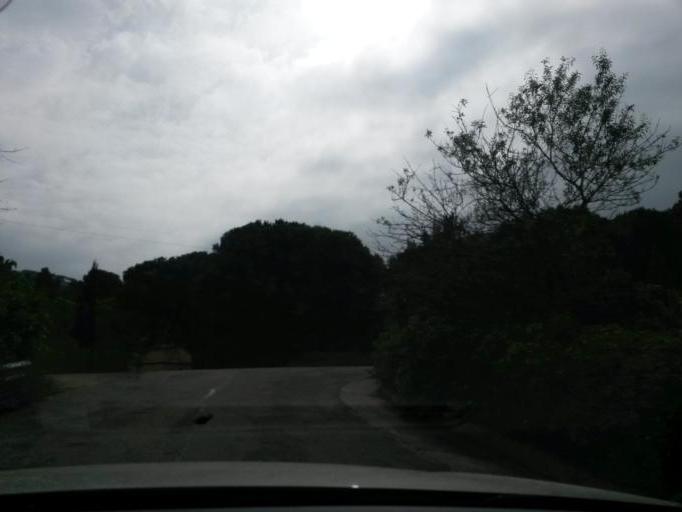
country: IT
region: Tuscany
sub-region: Provincia di Livorno
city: Capoliveri
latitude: 42.7415
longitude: 10.3694
